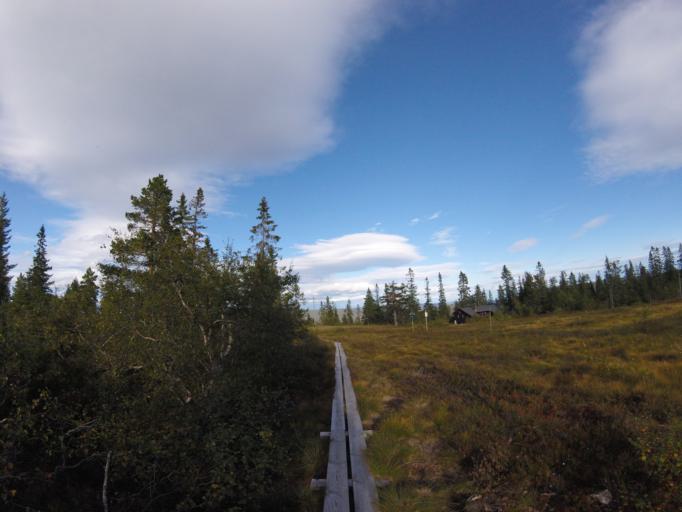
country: NO
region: Buskerud
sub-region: Flesberg
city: Lampeland
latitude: 59.7843
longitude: 9.4135
